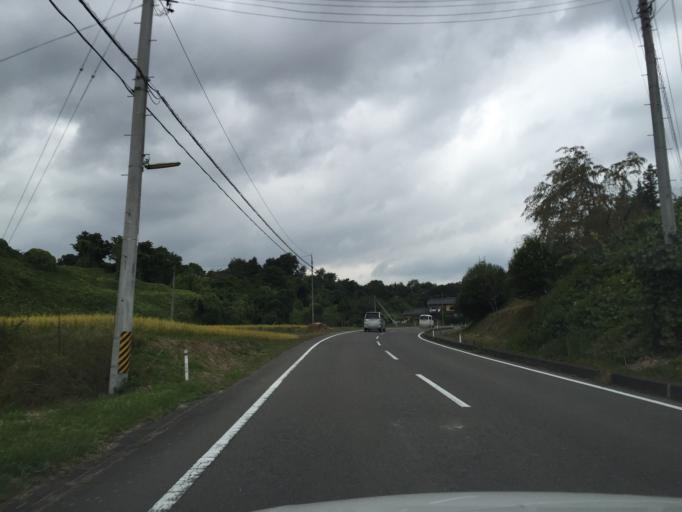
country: JP
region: Fukushima
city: Miharu
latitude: 37.4263
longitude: 140.5201
